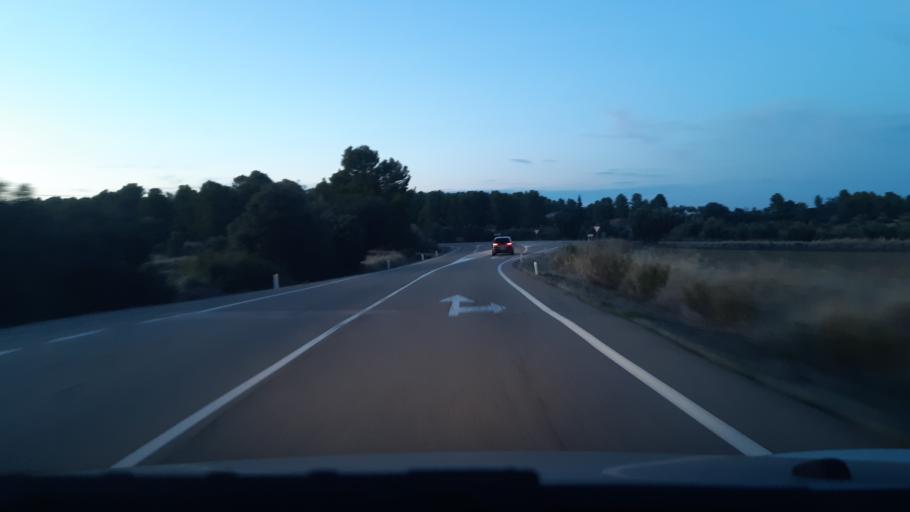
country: ES
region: Aragon
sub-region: Provincia de Teruel
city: Calaceite
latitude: 40.9774
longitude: 0.2027
